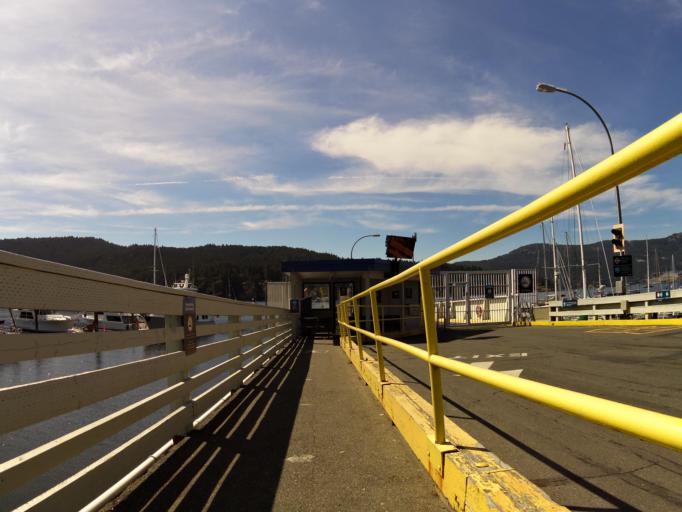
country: CA
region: British Columbia
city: North Saanich
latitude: 48.5776
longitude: -123.4664
